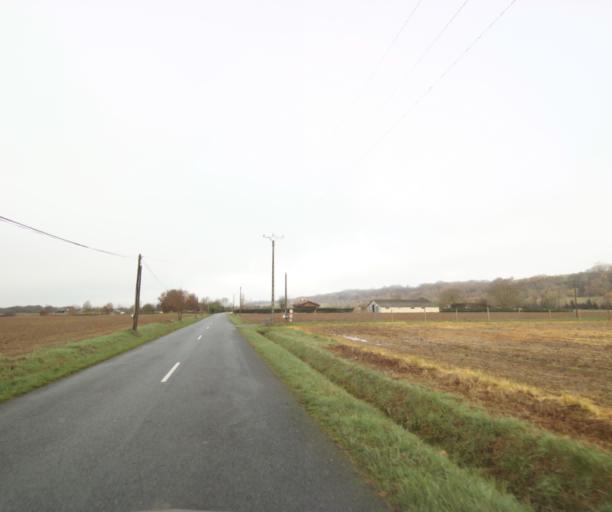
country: FR
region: Midi-Pyrenees
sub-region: Departement de la Haute-Garonne
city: Villemur-sur-Tarn
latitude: 43.8857
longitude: 1.4788
